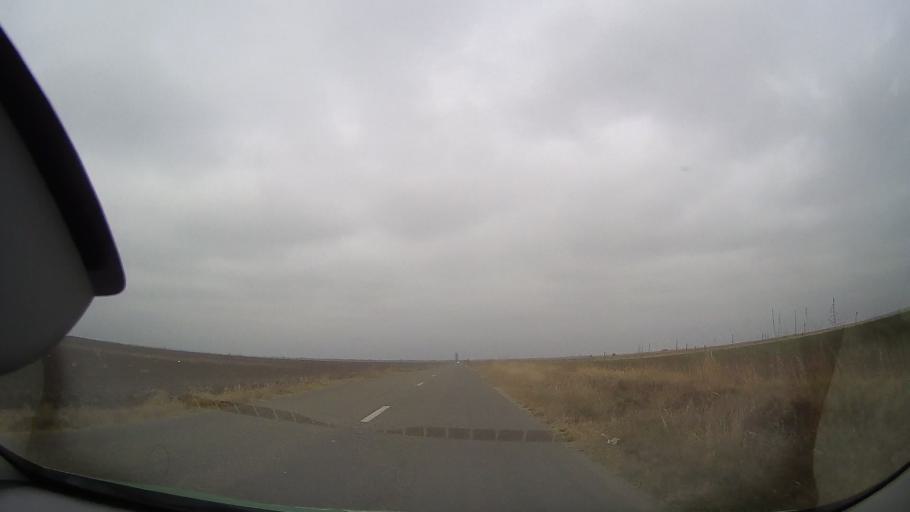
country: RO
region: Buzau
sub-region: Comuna Bradeanu
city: Bradeanu
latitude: 44.8954
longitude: 26.8733
